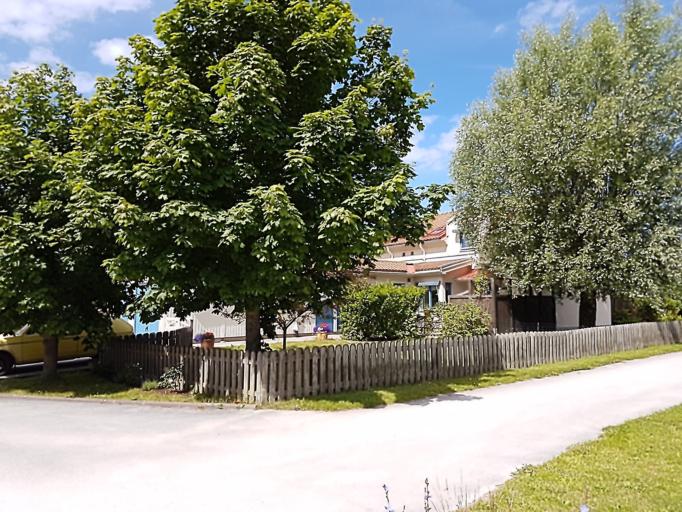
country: SE
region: Gotland
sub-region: Gotland
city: Visby
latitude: 57.6143
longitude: 18.3209
